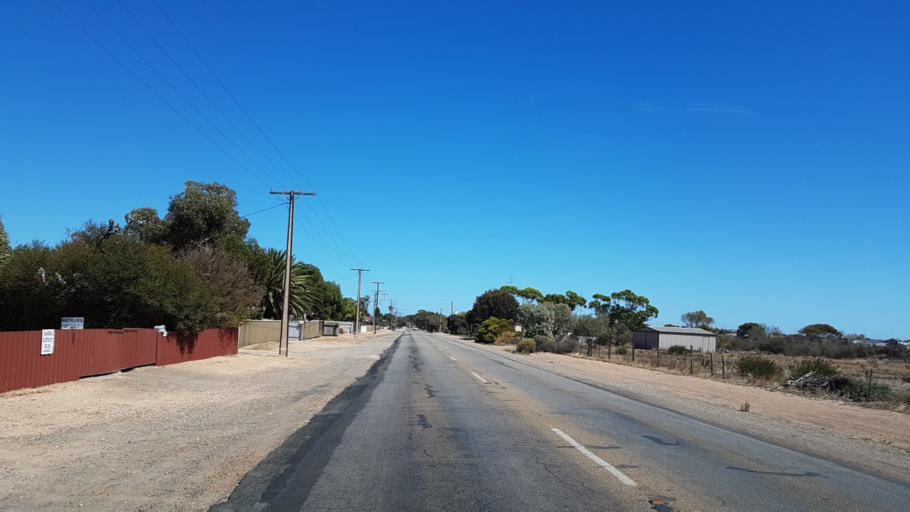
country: AU
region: South Australia
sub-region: Copper Coast
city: Wallaroo
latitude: -33.9380
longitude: 137.6459
